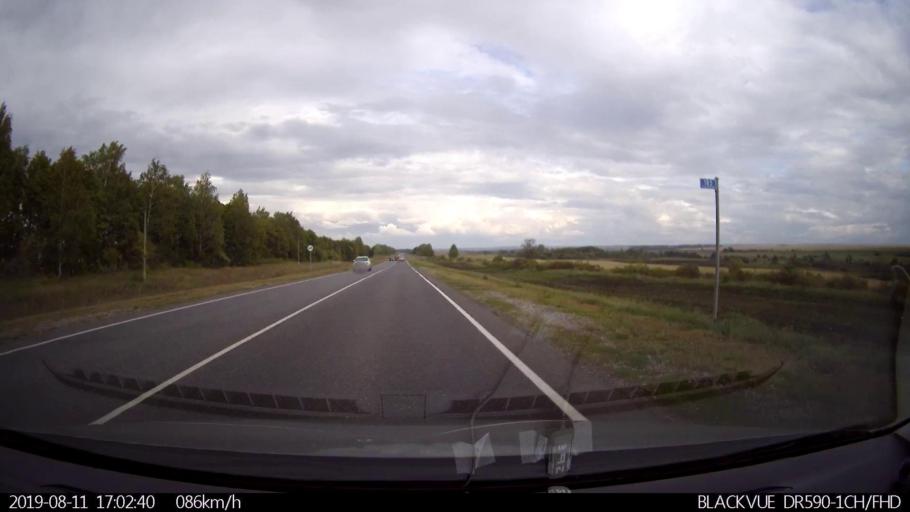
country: RU
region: Ulyanovsk
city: Mayna
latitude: 54.3054
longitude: 47.7200
